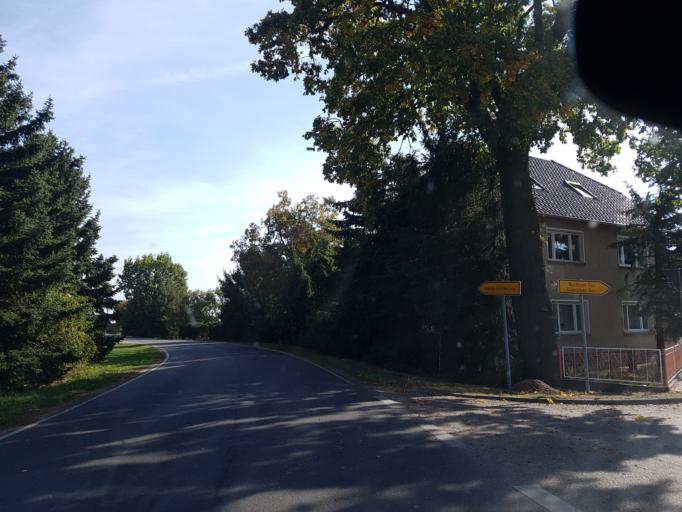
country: DE
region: Brandenburg
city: Doberlug-Kirchhain
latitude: 51.6699
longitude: 13.5113
